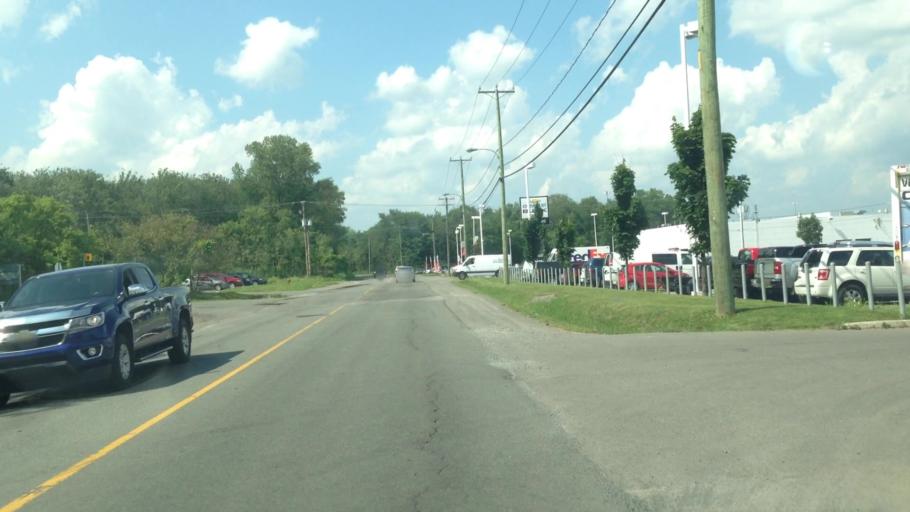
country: CA
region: Quebec
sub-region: Laurentides
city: Saint-Jerome
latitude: 45.7728
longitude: -74.0228
